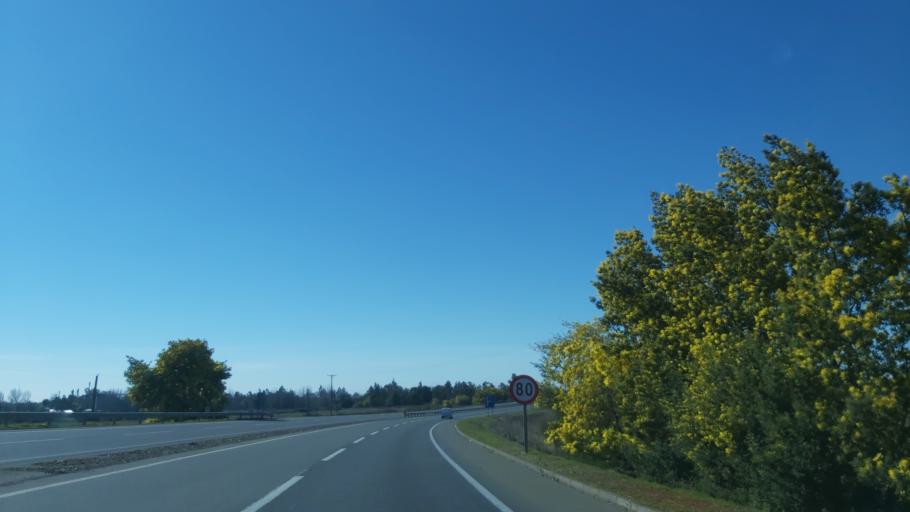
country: CL
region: Biobio
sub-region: Provincia de Nuble
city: Bulnes
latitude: -36.6539
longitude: -72.2385
